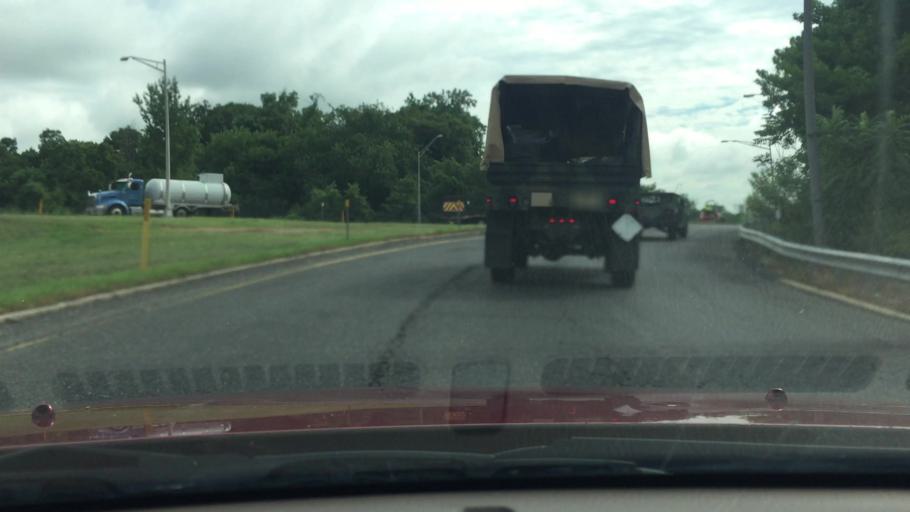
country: US
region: New Jersey
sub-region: Burlington County
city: Bordentown
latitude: 40.1234
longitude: -74.7059
